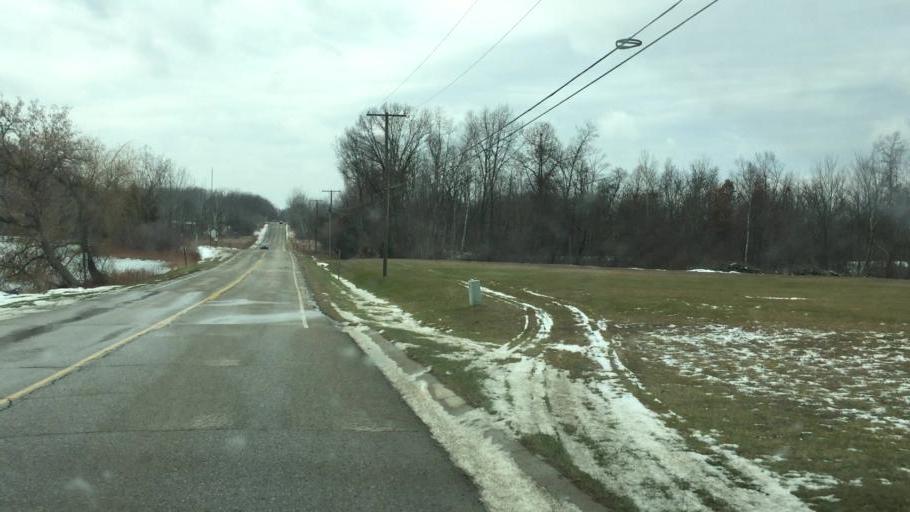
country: US
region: Michigan
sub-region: Lapeer County
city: Barnes Lake-Millers Lake
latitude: 43.1903
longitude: -83.3060
